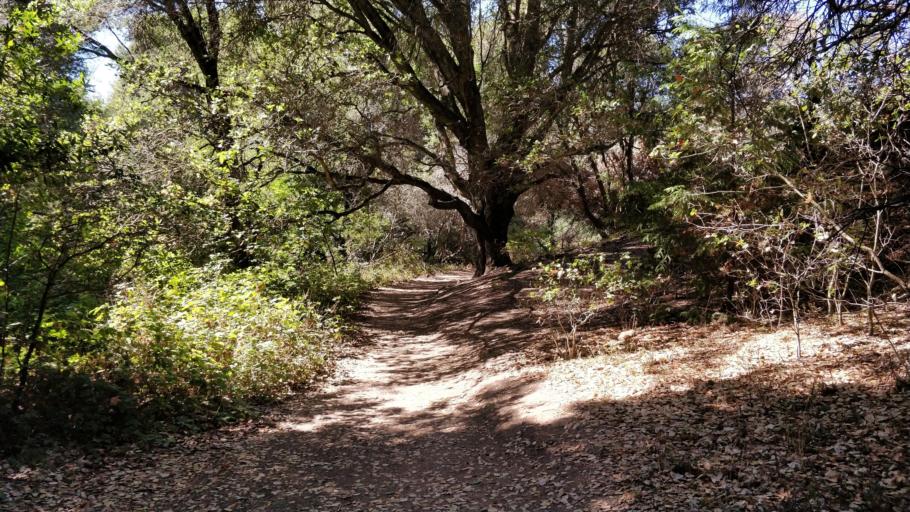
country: US
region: California
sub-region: Contra Costa County
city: Kensington
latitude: 37.9038
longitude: -122.2588
